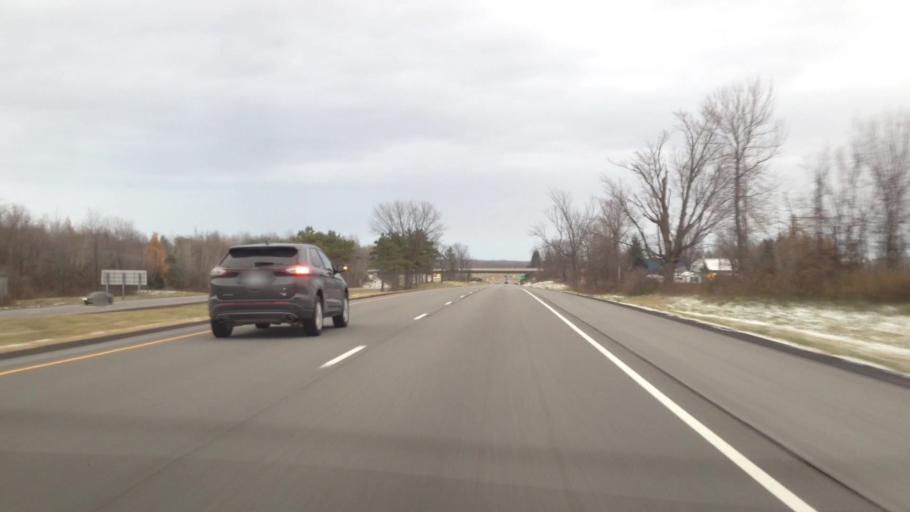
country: CA
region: Quebec
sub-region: Monteregie
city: Rigaud
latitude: 45.5403
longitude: -74.3961
